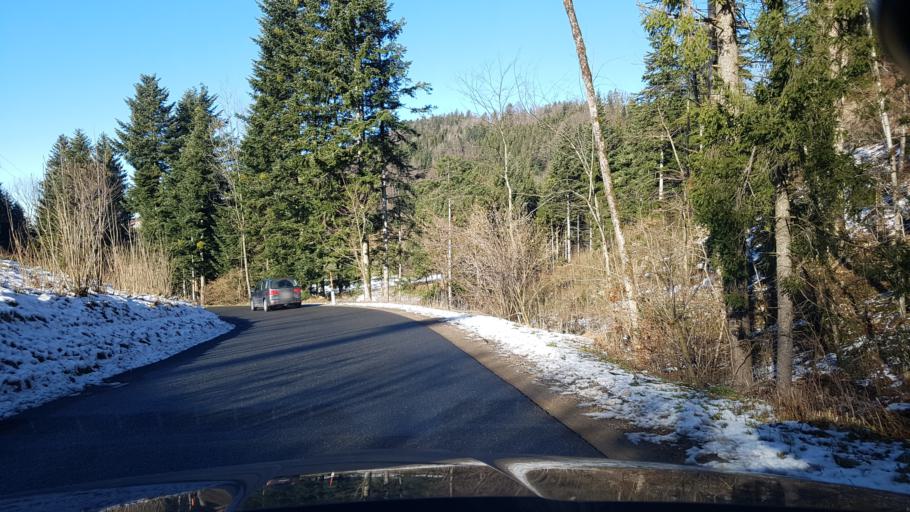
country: AT
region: Salzburg
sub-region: Politischer Bezirk Hallein
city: Golling an der Salzach
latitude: 47.6215
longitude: 13.1851
